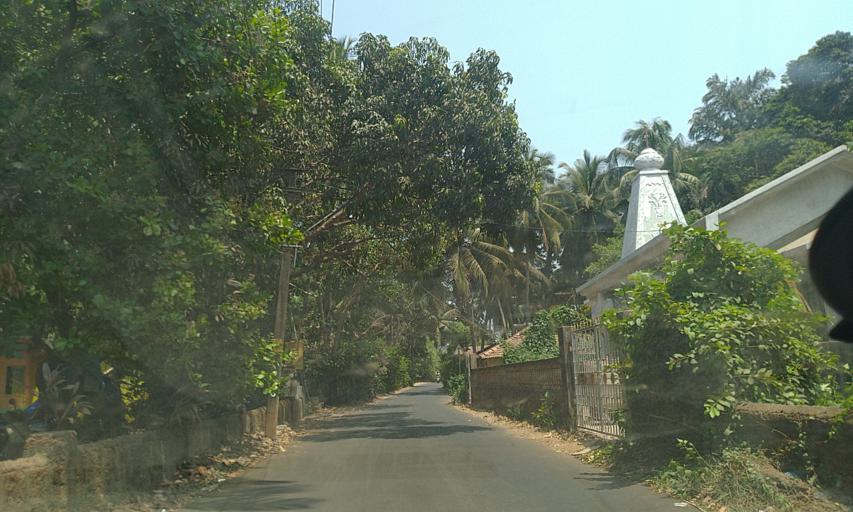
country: IN
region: Goa
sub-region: North Goa
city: Saligao
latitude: 15.5532
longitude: 73.8131
